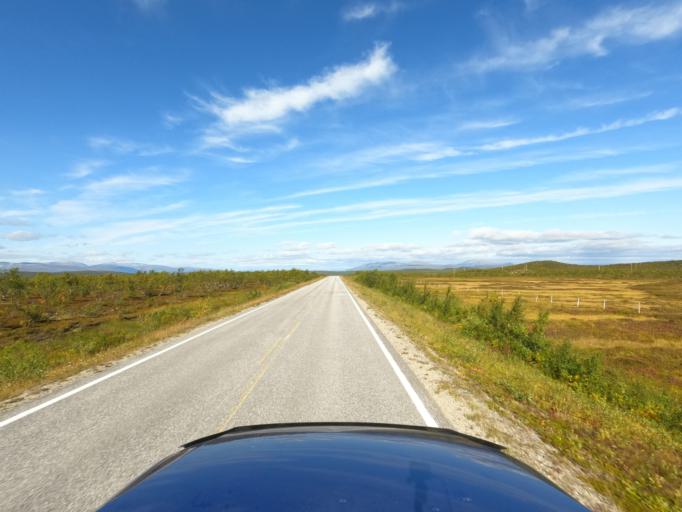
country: NO
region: Finnmark Fylke
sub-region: Karasjok
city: Karasjohka
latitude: 69.7202
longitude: 25.2377
